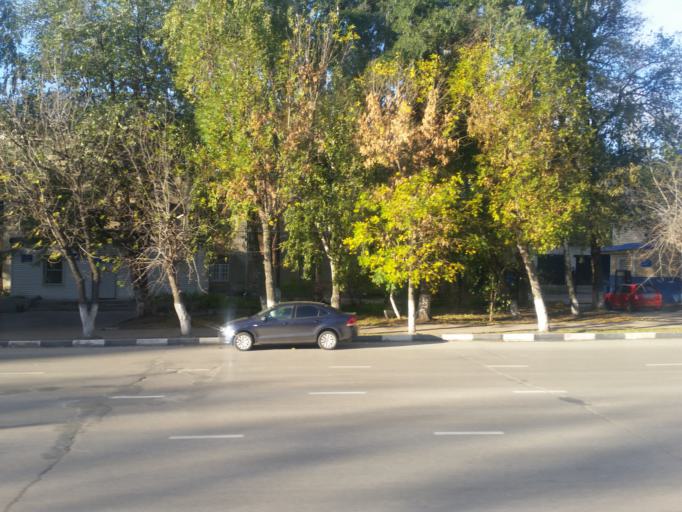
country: RU
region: Ulyanovsk
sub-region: Ulyanovskiy Rayon
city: Ulyanovsk
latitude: 54.3385
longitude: 48.3806
